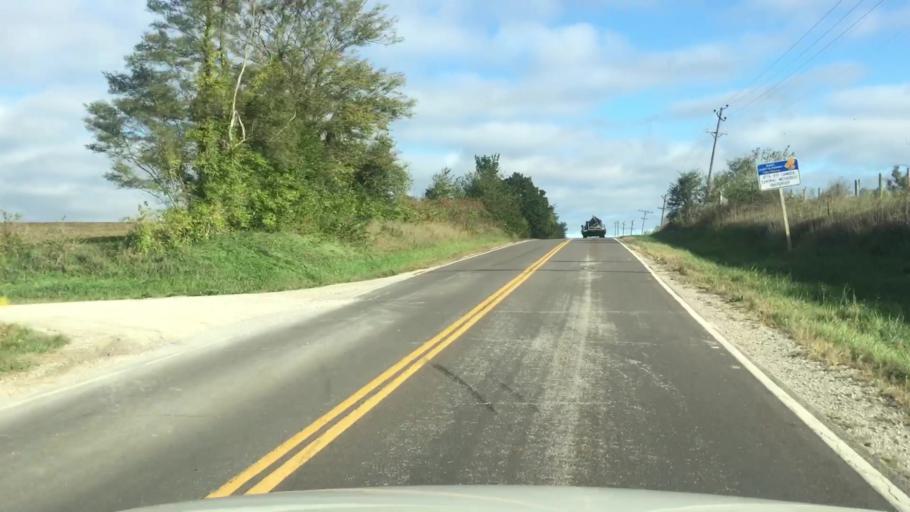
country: US
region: Missouri
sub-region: Howard County
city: New Franklin
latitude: 39.0789
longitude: -92.7456
